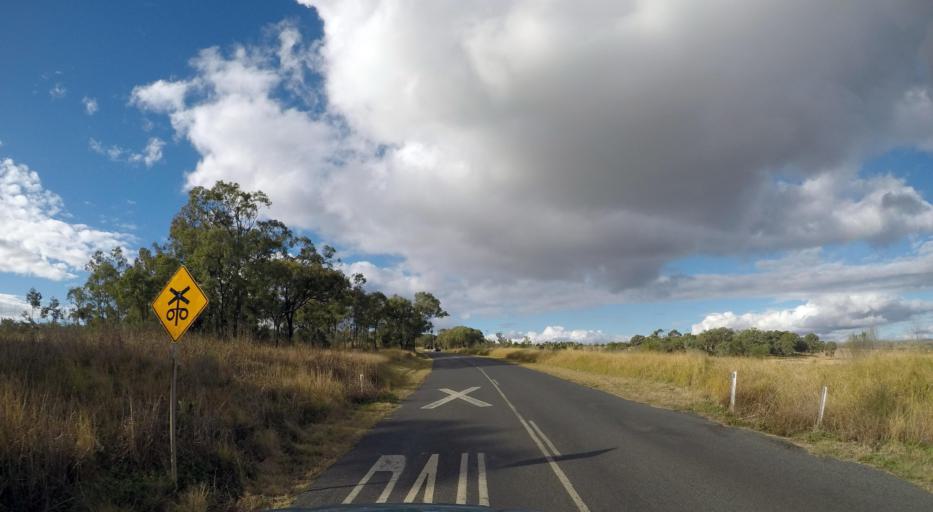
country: AU
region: Queensland
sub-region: Toowoomba
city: Westbrook
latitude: -27.7033
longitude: 151.6579
